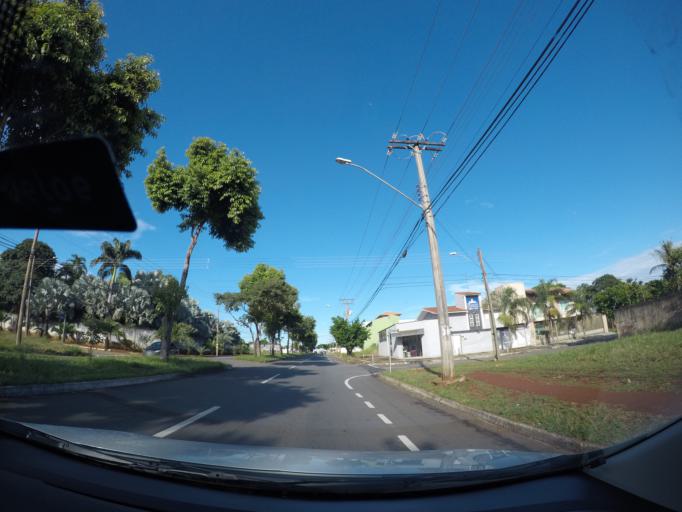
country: BR
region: Goias
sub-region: Goiania
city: Goiania
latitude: -16.7343
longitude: -49.3046
